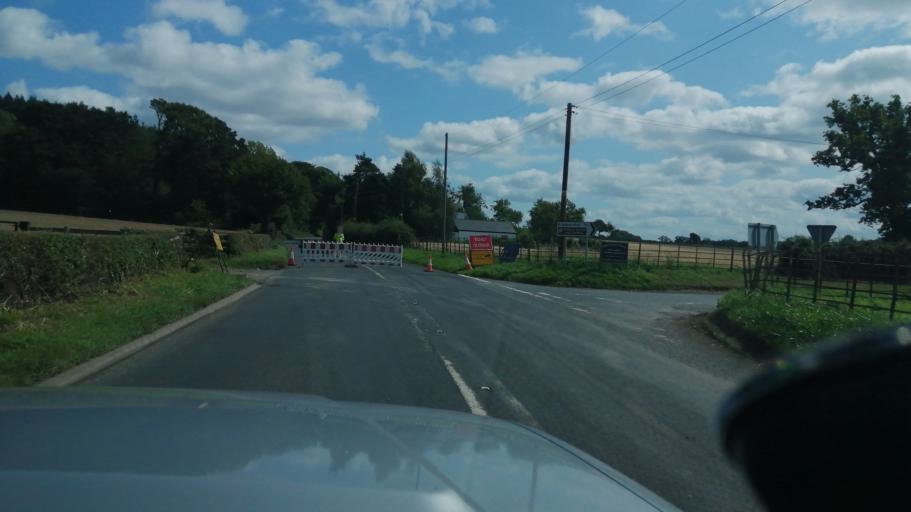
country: GB
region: England
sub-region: Herefordshire
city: Kinnersley
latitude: 52.1101
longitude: -2.9652
